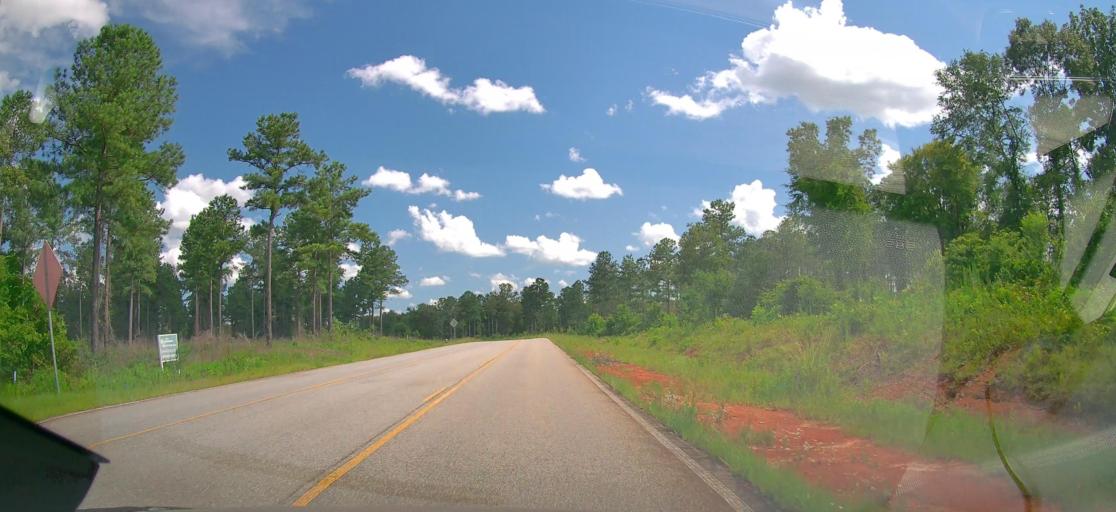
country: US
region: Georgia
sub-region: Peach County
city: Byron
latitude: 32.6005
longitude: -83.7407
